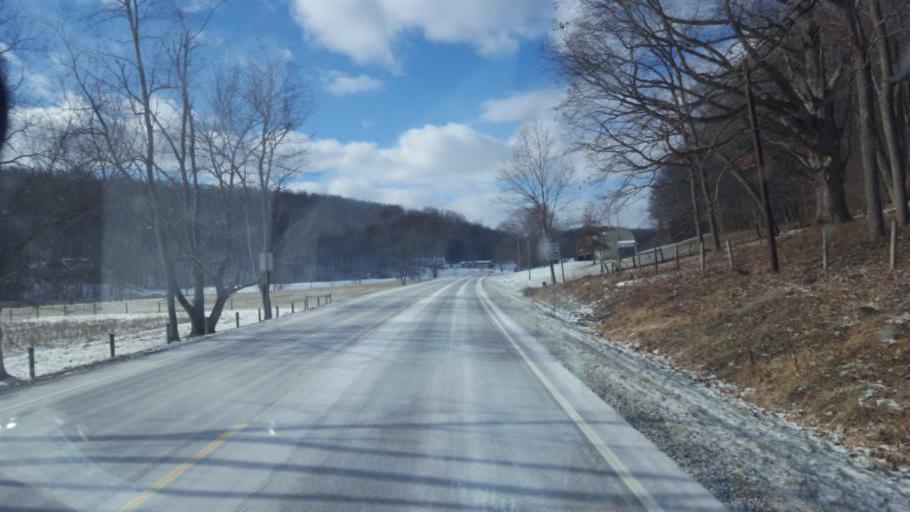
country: US
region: Ohio
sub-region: Knox County
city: Oak Hill
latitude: 40.3383
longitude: -82.0752
